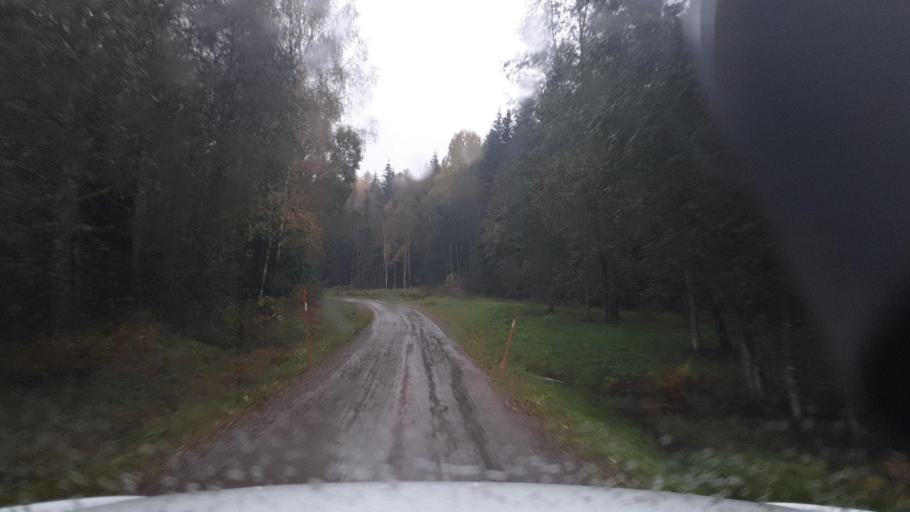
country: SE
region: Vaermland
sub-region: Eda Kommun
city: Amotfors
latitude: 59.7868
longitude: 12.4273
